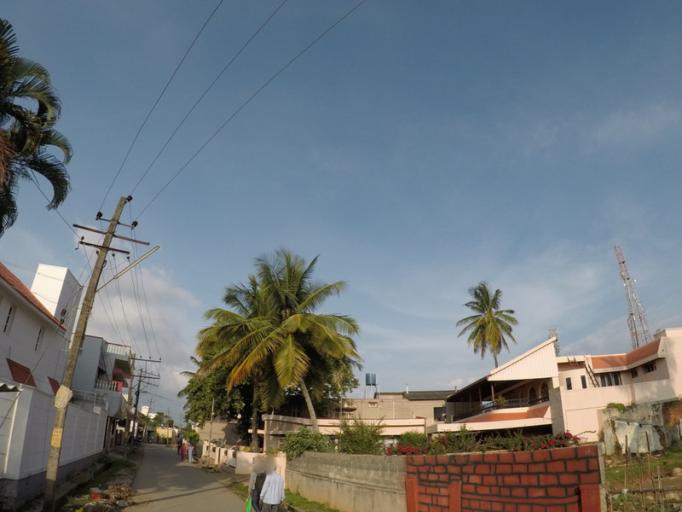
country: IN
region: Karnataka
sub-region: Chikmagalur
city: Chikmagalur
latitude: 13.3098
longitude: 75.7783
